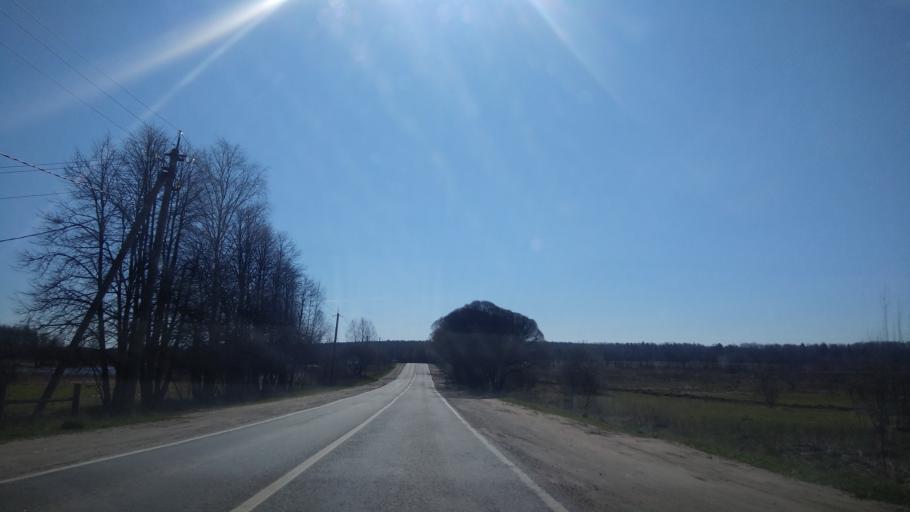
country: RU
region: Moskovskaya
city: Pravdinskiy
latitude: 56.0462
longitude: 37.8808
